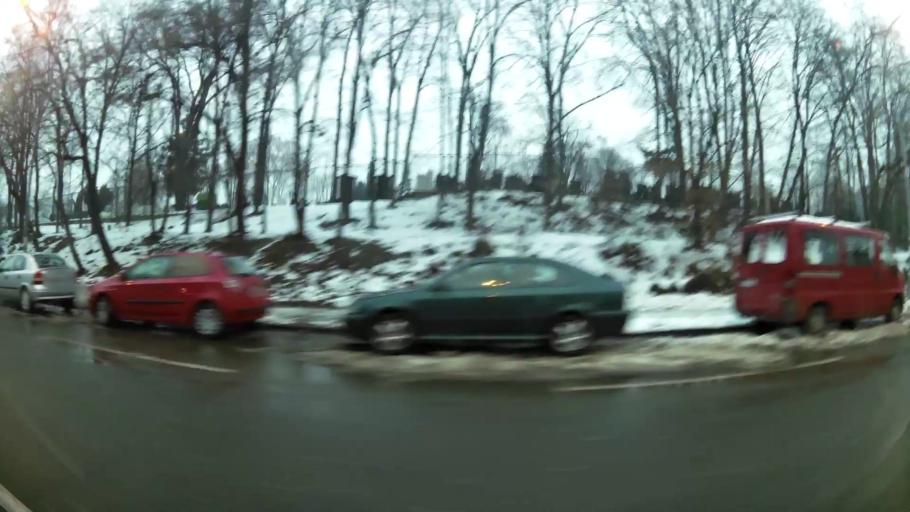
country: RS
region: Central Serbia
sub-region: Belgrade
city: Vozdovac
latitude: 44.7728
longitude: 20.4928
